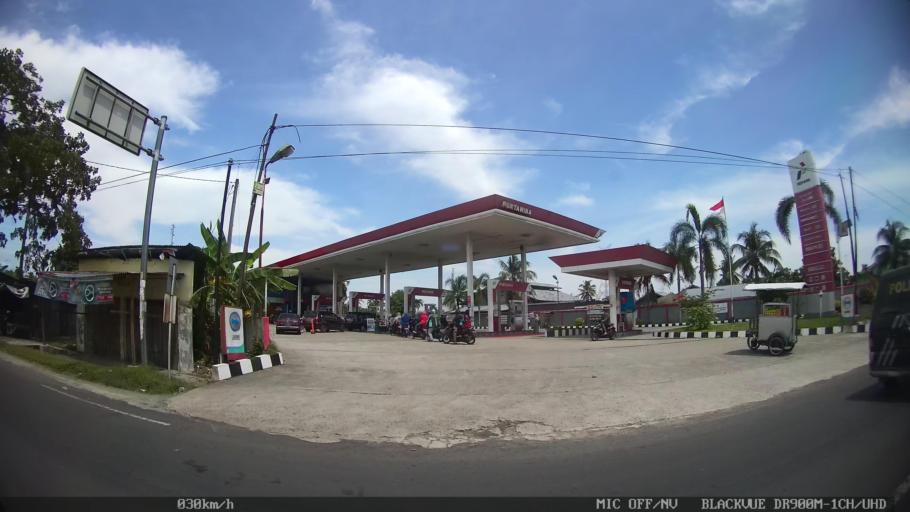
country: ID
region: North Sumatra
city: Binjai
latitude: 3.6269
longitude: 98.5077
